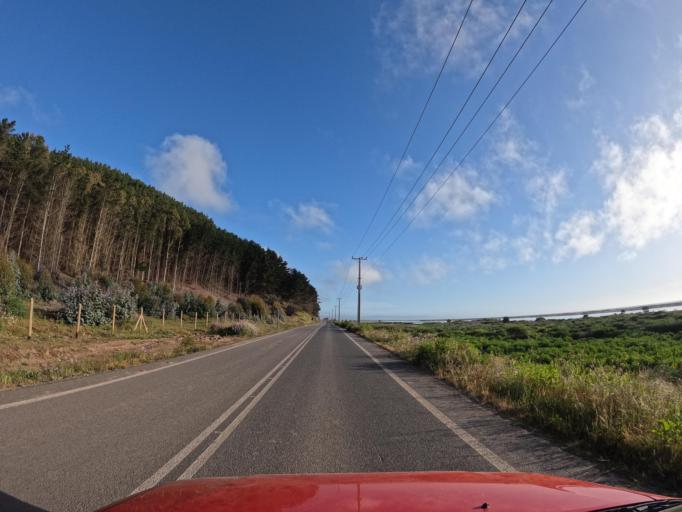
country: CL
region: Maule
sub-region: Provincia de Talca
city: Constitucion
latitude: -34.9902
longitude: -72.1788
